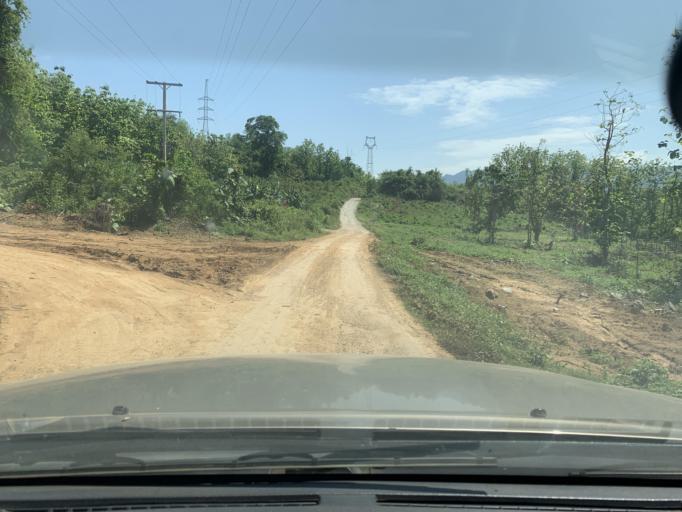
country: LA
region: Louangphabang
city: Louangphabang
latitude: 19.8974
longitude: 102.2113
